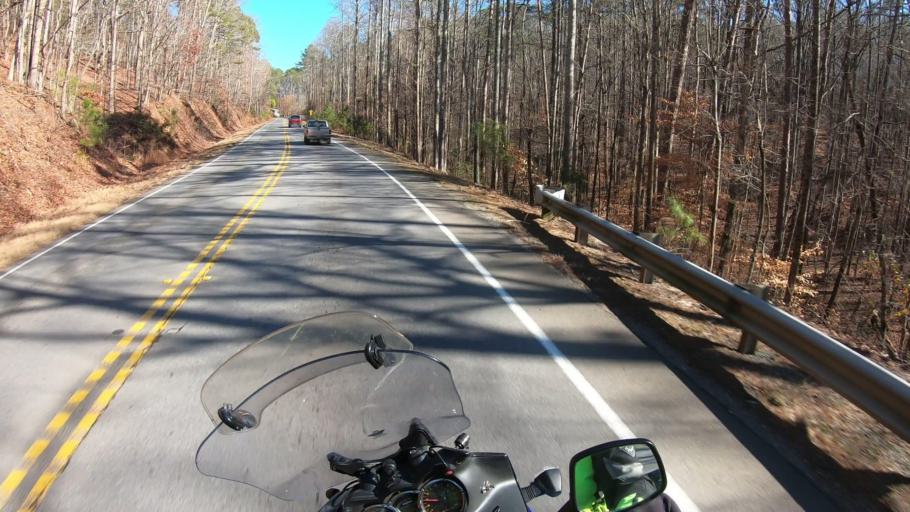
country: US
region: Georgia
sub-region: Gilmer County
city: Ellijay
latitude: 34.5776
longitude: -84.6223
